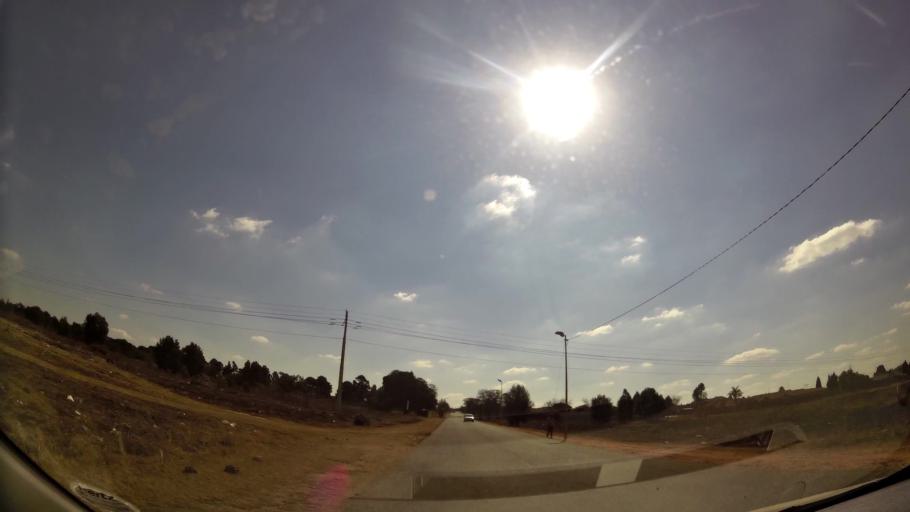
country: ZA
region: Gauteng
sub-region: West Rand District Municipality
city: Randfontein
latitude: -26.1775
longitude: 27.7481
